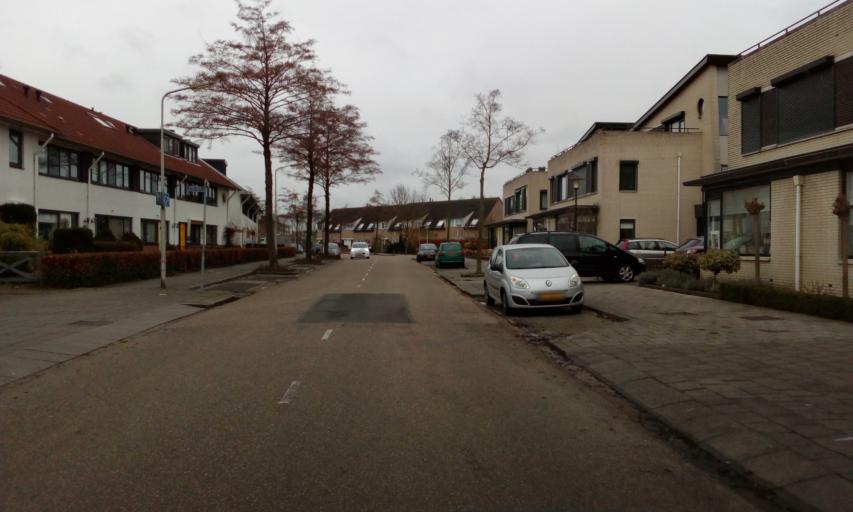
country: NL
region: South Holland
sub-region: Gemeente Alblasserdam
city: Alblasserdam
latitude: 51.8722
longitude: 4.6584
